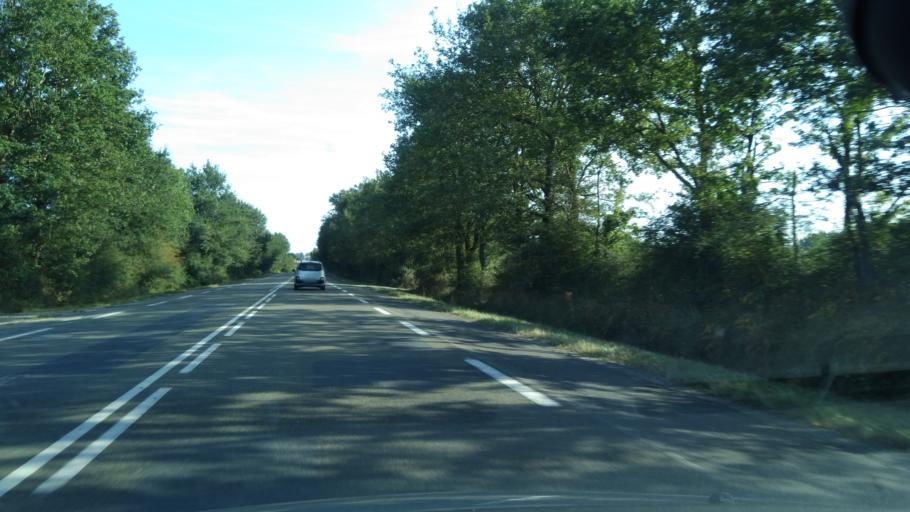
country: FR
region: Pays de la Loire
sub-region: Departement de la Mayenne
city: Entrammes
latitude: 47.9847
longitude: -0.7117
